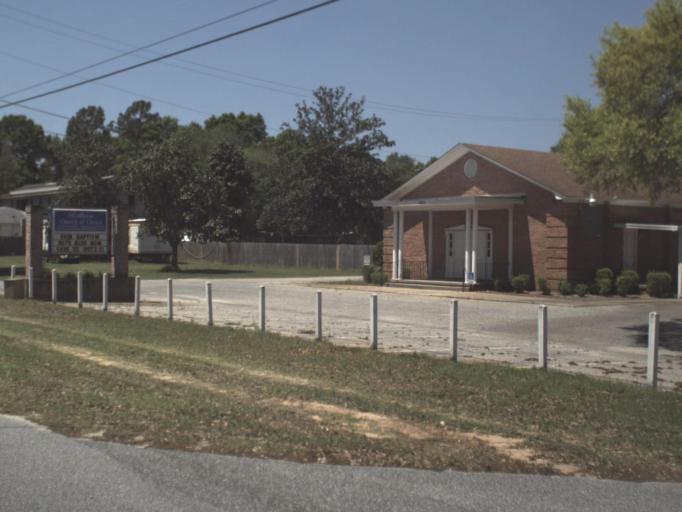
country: US
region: Florida
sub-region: Escambia County
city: Bellview
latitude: 30.4614
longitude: -87.3133
